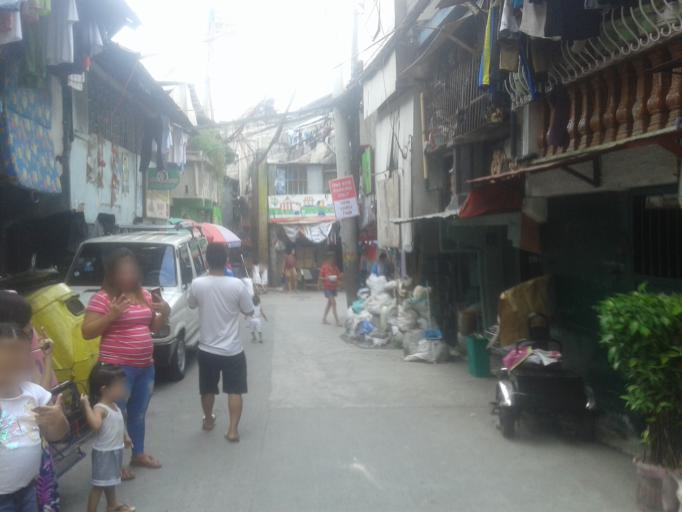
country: PH
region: Metro Manila
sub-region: Mandaluyong
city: Mandaluyong City
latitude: 14.5856
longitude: 121.0397
